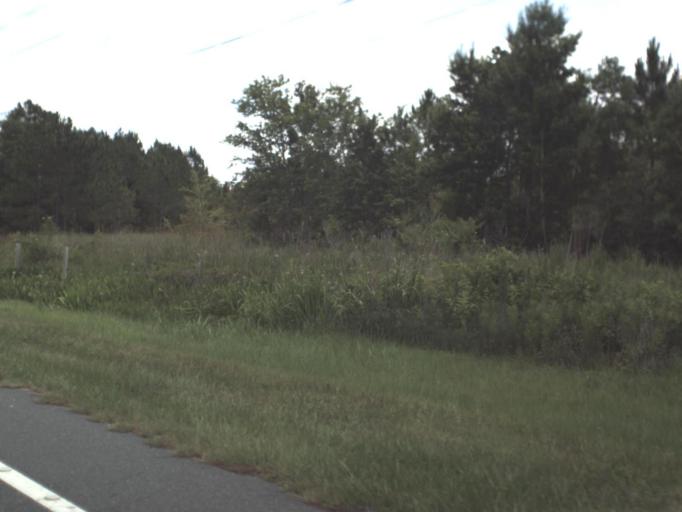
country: US
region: Florida
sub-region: Levy County
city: Chiefland
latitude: 29.1945
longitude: -83.0016
